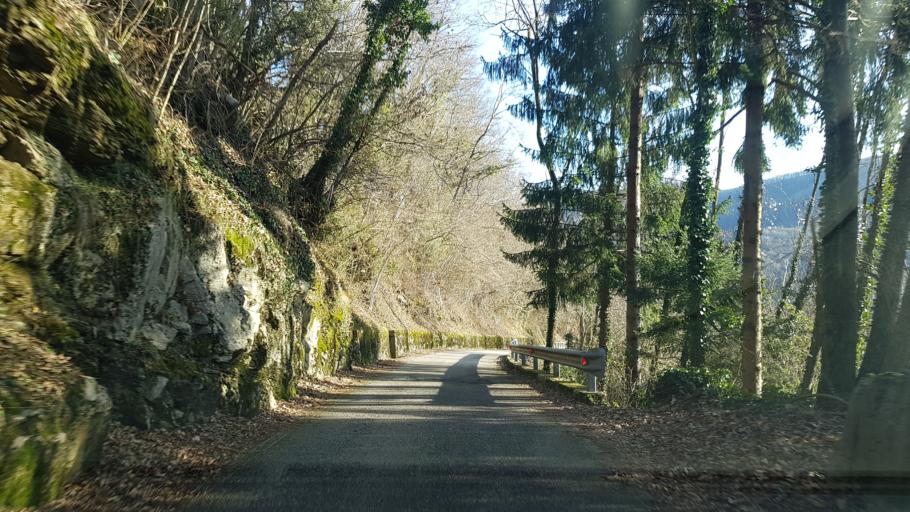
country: IT
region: Friuli Venezia Giulia
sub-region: Provincia di Udine
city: Clodig
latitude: 46.1613
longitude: 13.5816
